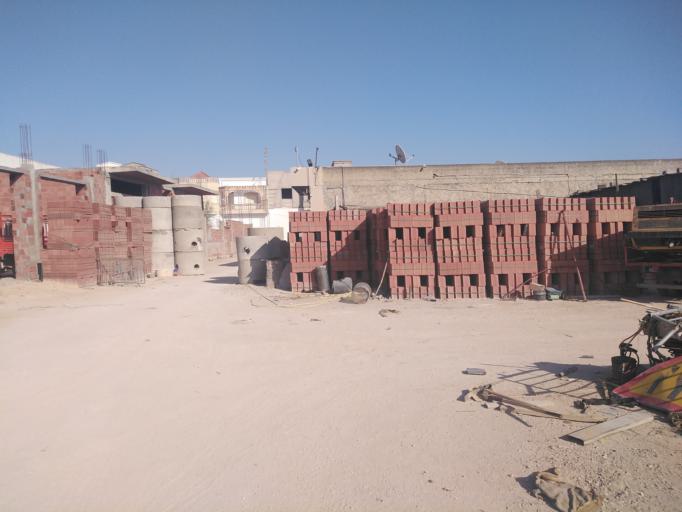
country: TN
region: Al Mahdiyah
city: El Jem
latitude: 35.2898
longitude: 10.6995
